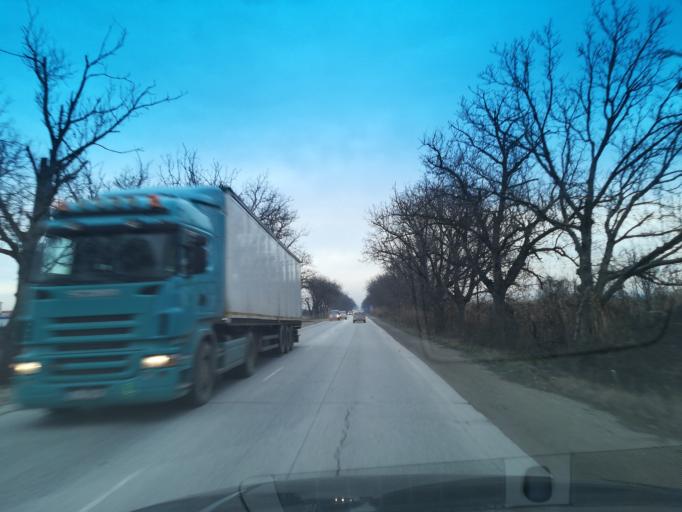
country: BG
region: Plovdiv
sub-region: Obshtina Plovdiv
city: Plovdiv
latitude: 42.0920
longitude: 24.7120
